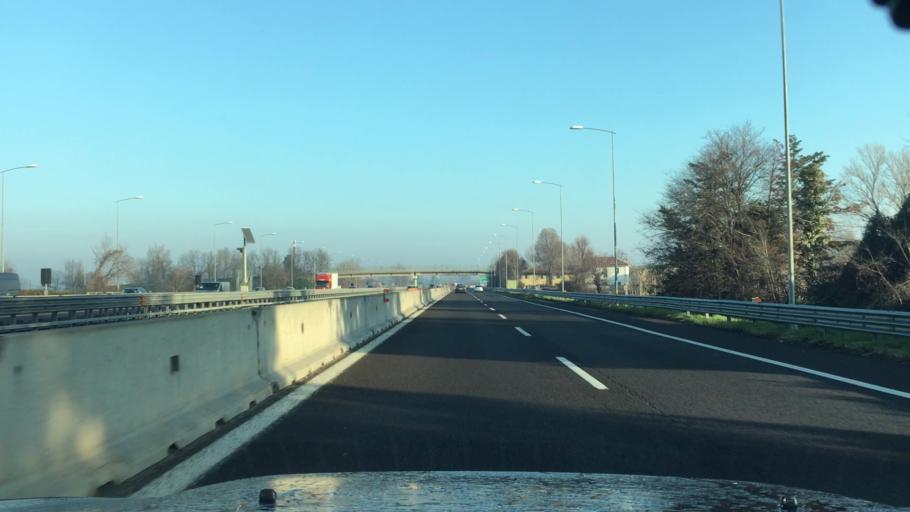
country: IT
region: Emilia-Romagna
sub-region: Provincia di Bologna
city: Casalecchio di Reno
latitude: 44.4995
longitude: 11.2720
